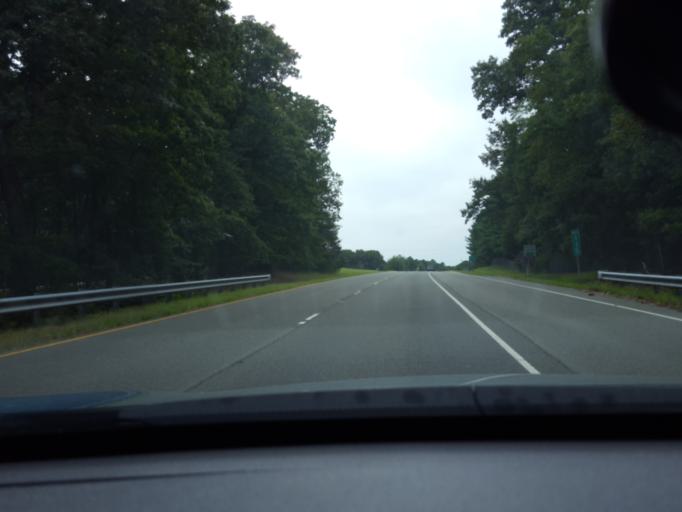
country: US
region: Virginia
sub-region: Caroline County
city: Bowling Green
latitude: 38.0737
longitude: -77.3181
